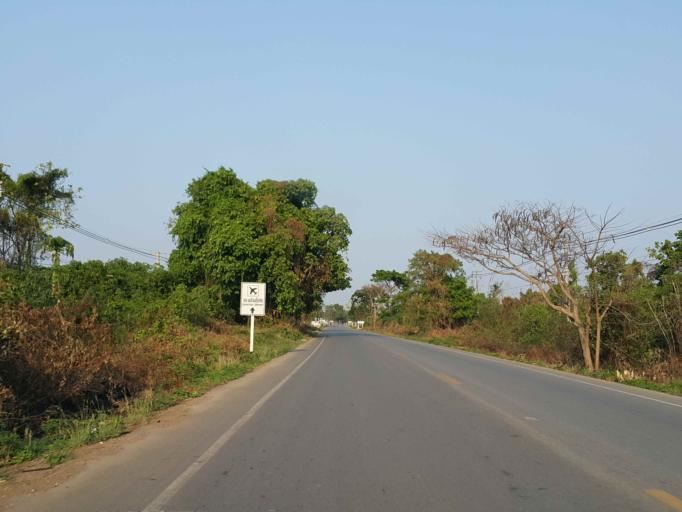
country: TH
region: Sukhothai
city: Sawankhalok
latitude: 17.3091
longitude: 99.7906
